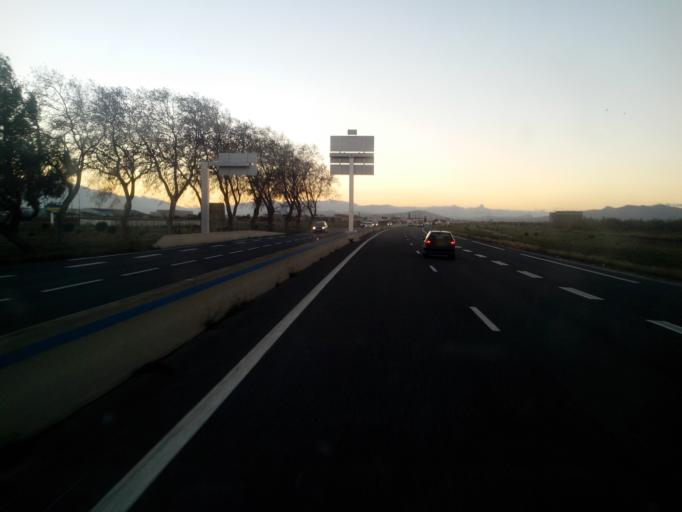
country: FR
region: Languedoc-Roussillon
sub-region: Departement des Pyrenees-Orientales
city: Saint-Hippolyte
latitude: 42.7776
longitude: 2.9591
